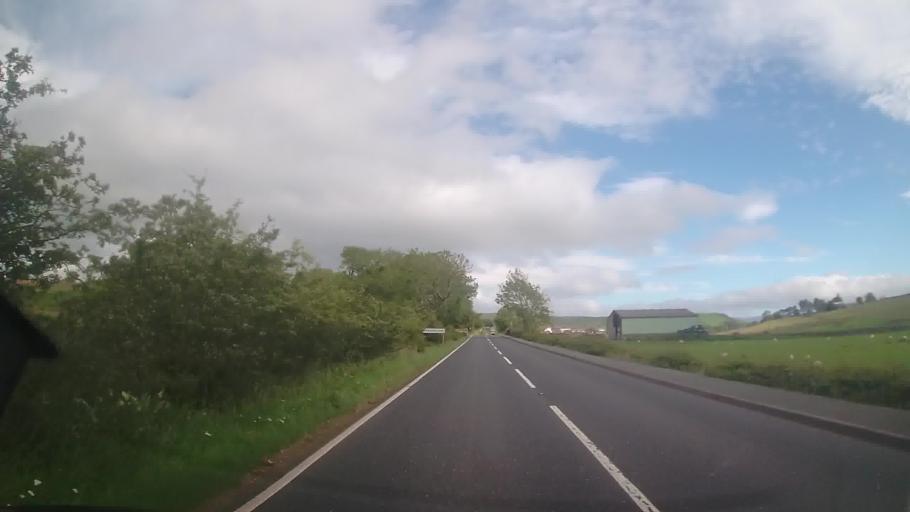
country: GB
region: Wales
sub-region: Conwy
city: Llangwm
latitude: 53.0291
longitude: -3.5732
